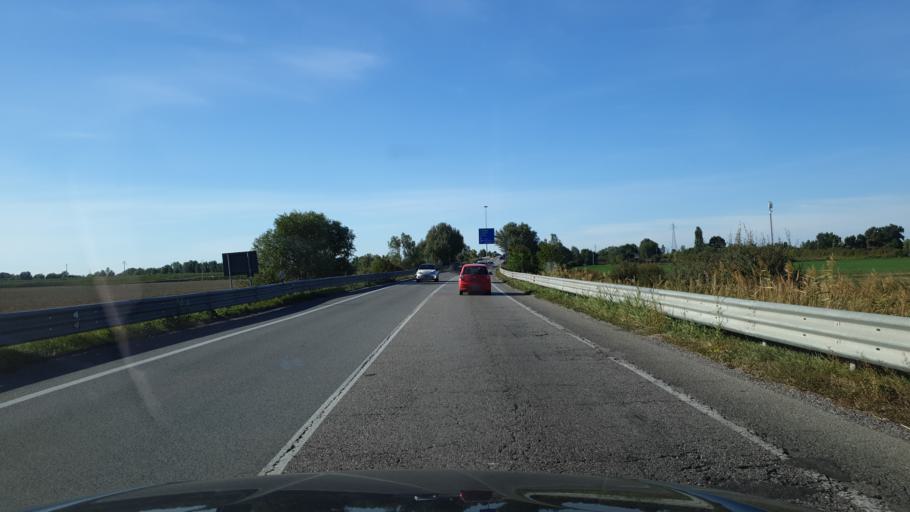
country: IT
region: Emilia-Romagna
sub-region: Provincia di Ravenna
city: Savio
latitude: 44.2978
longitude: 12.2944
